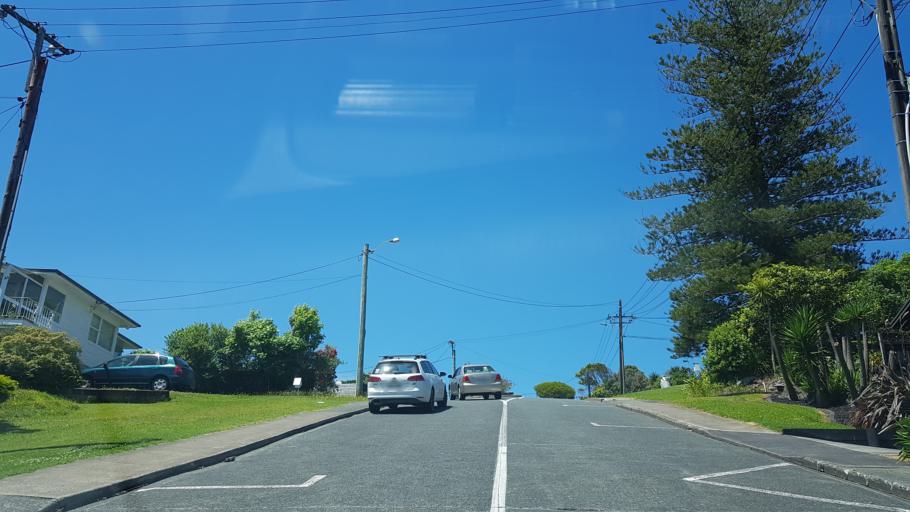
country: NZ
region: Auckland
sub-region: Auckland
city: North Shore
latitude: -36.8091
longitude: 174.7405
